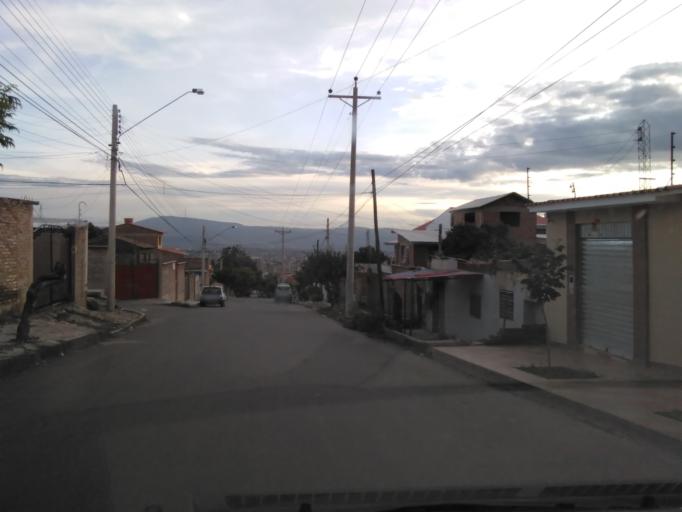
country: BO
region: Cochabamba
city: Cochabamba
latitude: -17.3579
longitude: -66.1608
